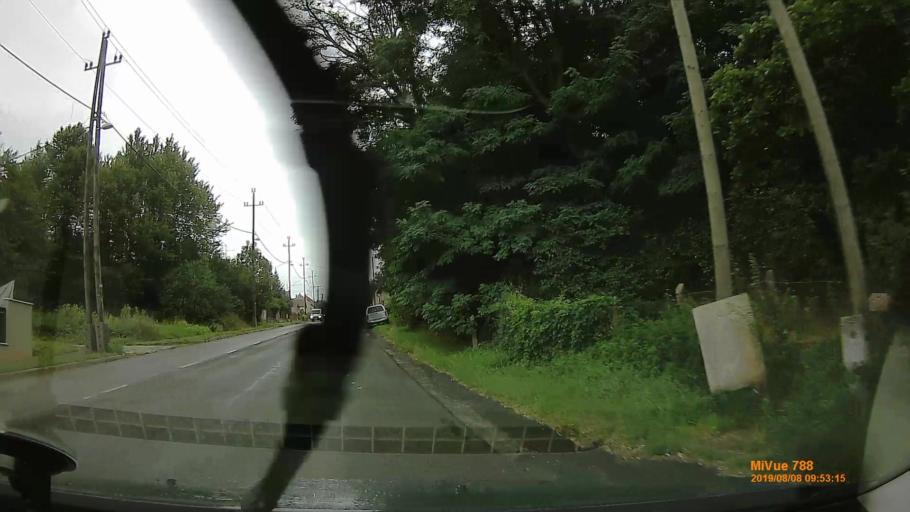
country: HU
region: Vas
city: Vasvar
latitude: 47.0455
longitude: 16.8076
